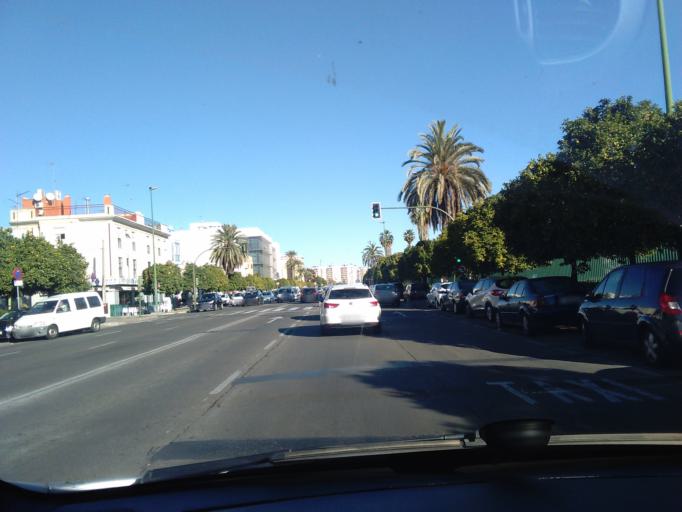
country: ES
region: Andalusia
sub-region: Provincia de Sevilla
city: Sevilla
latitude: 37.3835
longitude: -5.9598
